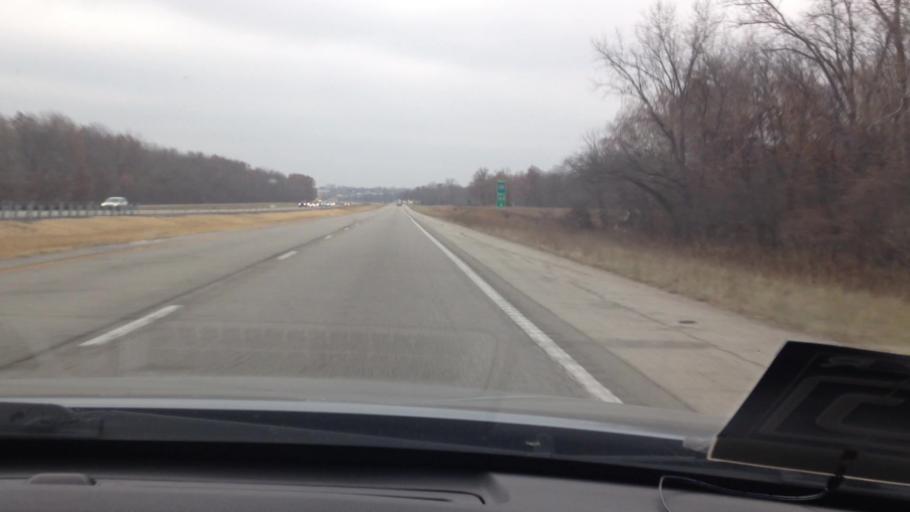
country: US
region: Missouri
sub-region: Cass County
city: Peculiar
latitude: 38.6908
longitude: -94.4270
